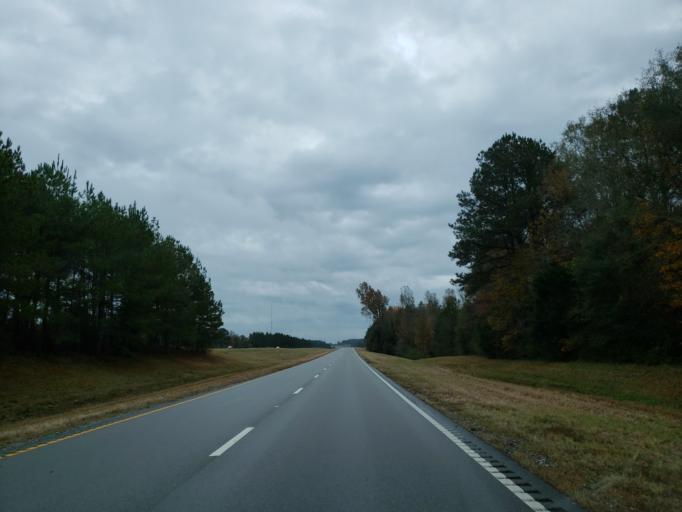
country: US
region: Mississippi
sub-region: Wayne County
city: Waynesboro
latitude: 31.6940
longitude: -88.7182
